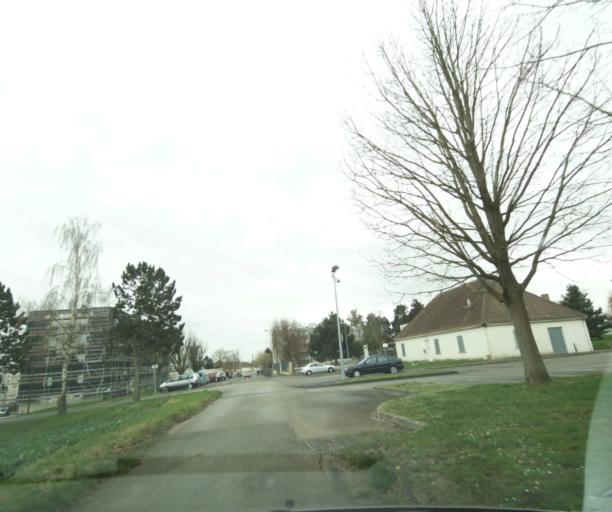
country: FR
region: Picardie
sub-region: Departement de l'Oise
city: Noyon
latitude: 49.5861
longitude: 3.0061
